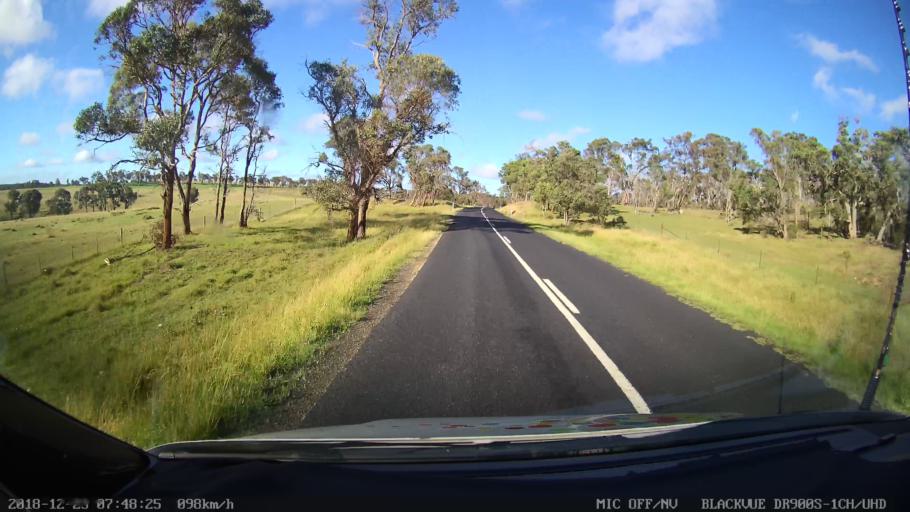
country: AU
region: New South Wales
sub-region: Armidale Dumaresq
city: Armidale
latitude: -30.5320
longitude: 151.8861
